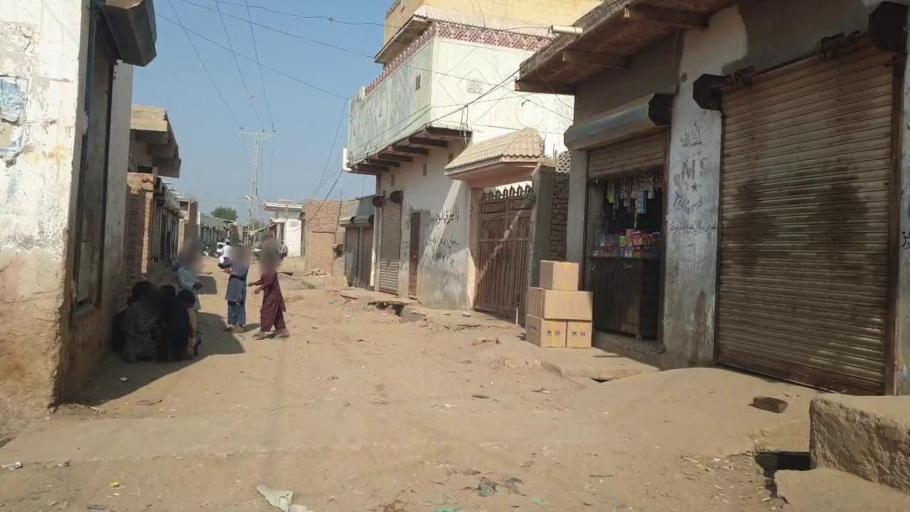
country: PK
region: Sindh
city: Jamshoro
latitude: 25.4366
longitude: 68.2805
